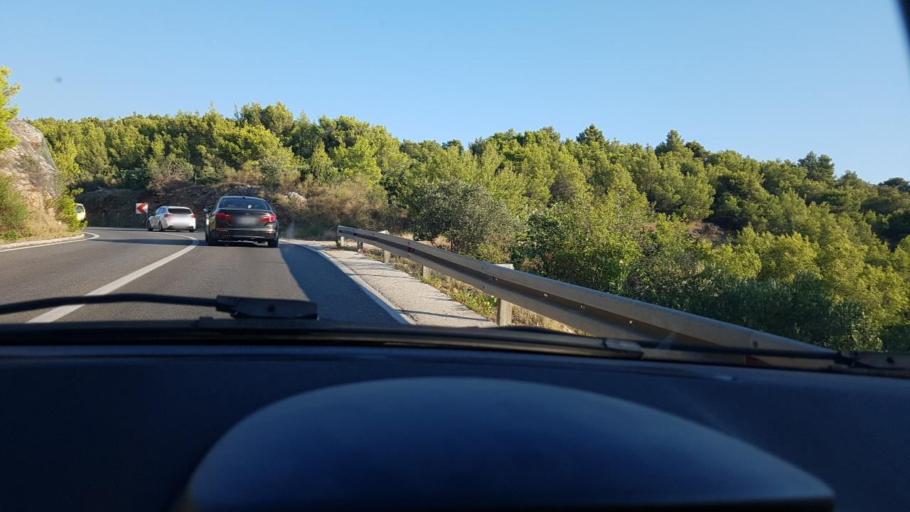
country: HR
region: Sibensko-Kniniska
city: Murter
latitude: 43.7971
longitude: 15.6170
